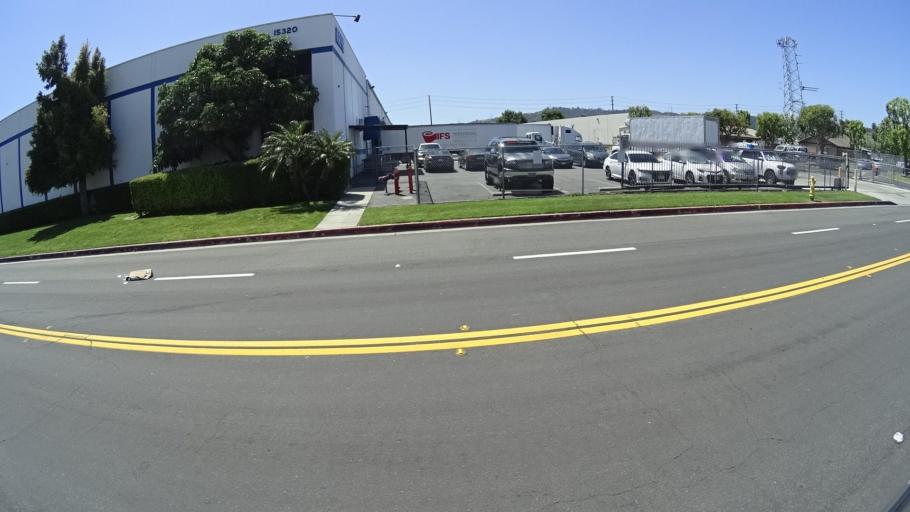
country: US
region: California
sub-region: Los Angeles County
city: La Puente
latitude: 34.0196
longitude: -117.9694
